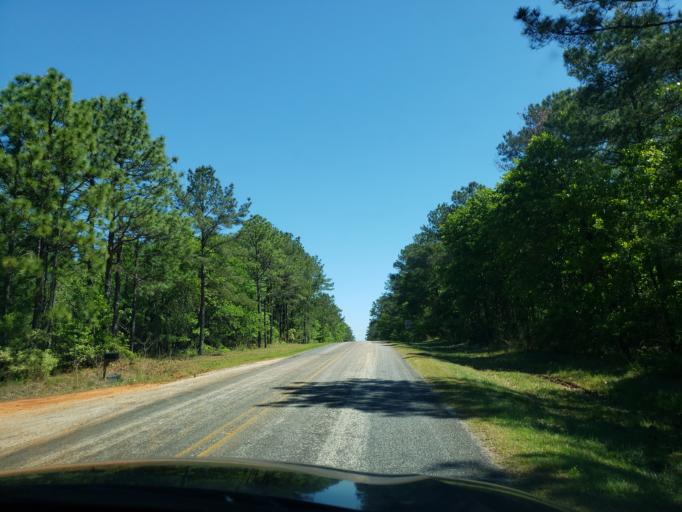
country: US
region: Alabama
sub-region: Elmore County
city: Eclectic
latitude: 32.6930
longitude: -85.8978
